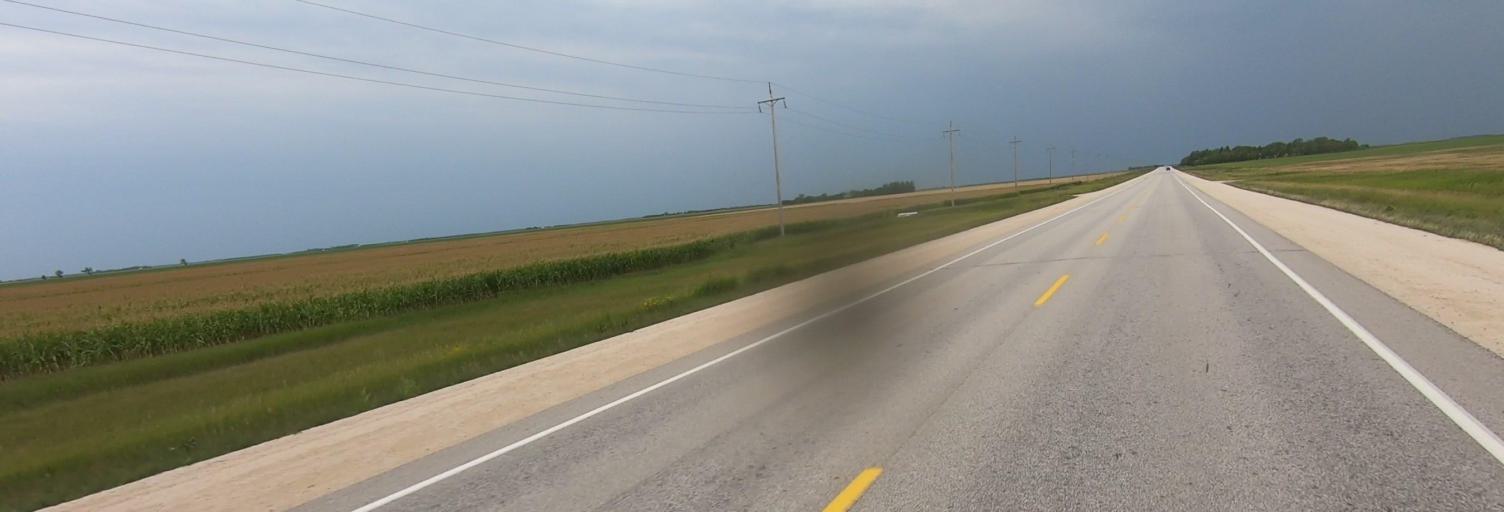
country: CA
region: Manitoba
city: Headingley
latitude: 49.7683
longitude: -97.3738
